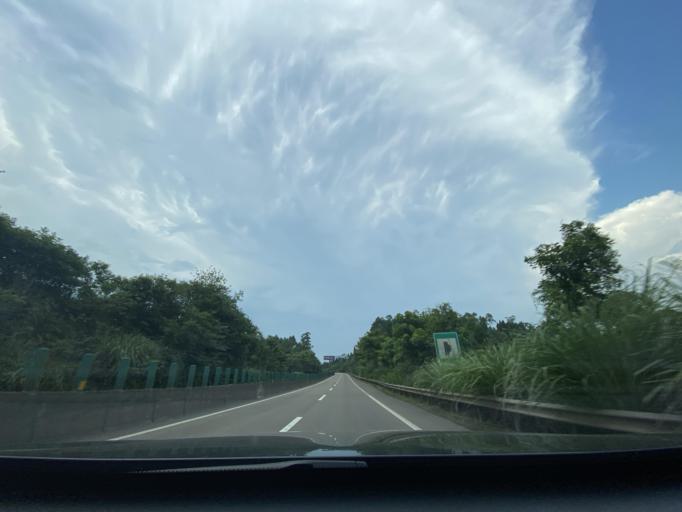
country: CN
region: Sichuan
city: Neijiang
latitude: 29.6552
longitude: 104.9836
